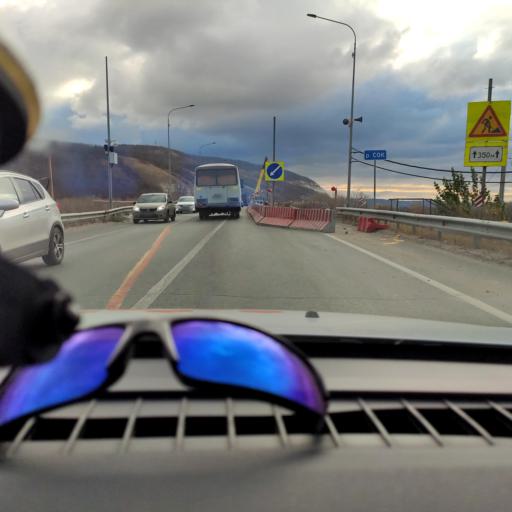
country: RU
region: Samara
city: Volzhskiy
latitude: 53.4133
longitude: 50.1349
